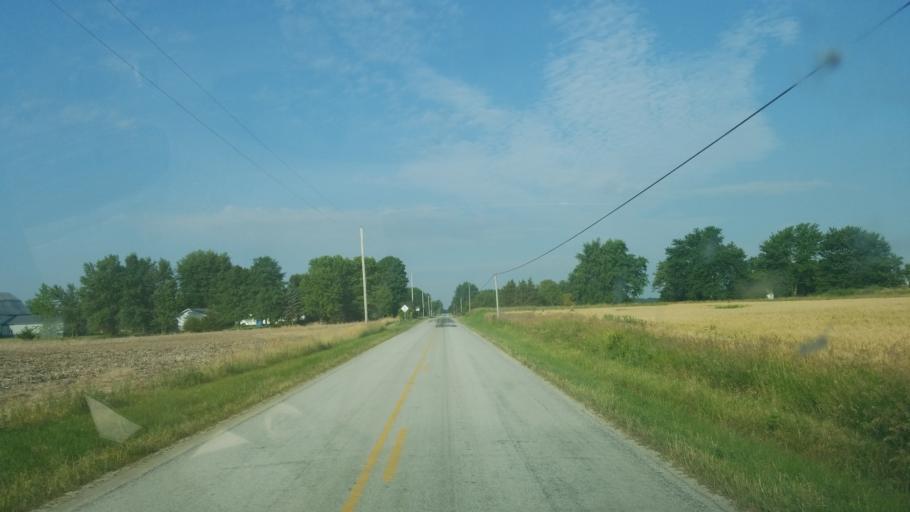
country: US
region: Ohio
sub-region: Hardin County
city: Kenton
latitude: 40.6270
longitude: -83.7043
